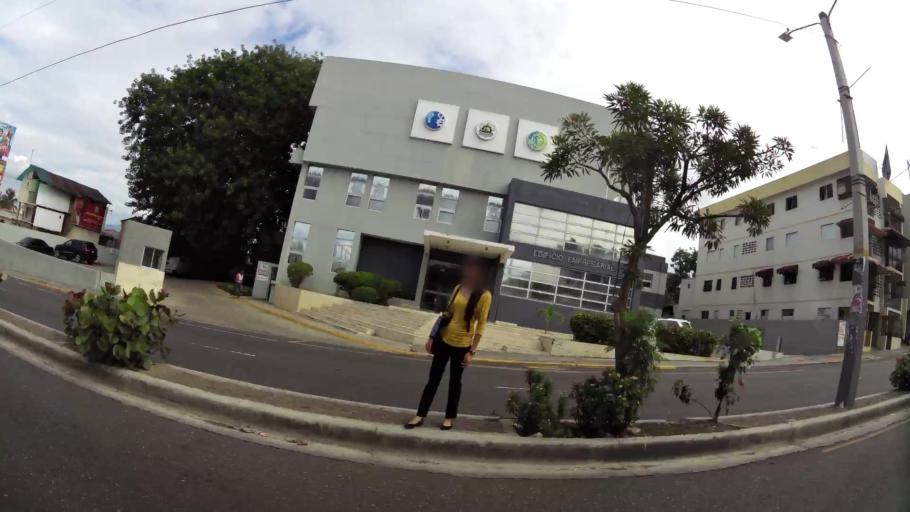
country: DO
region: Santiago
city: Santiago de los Caballeros
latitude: 19.4527
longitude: -70.6961
